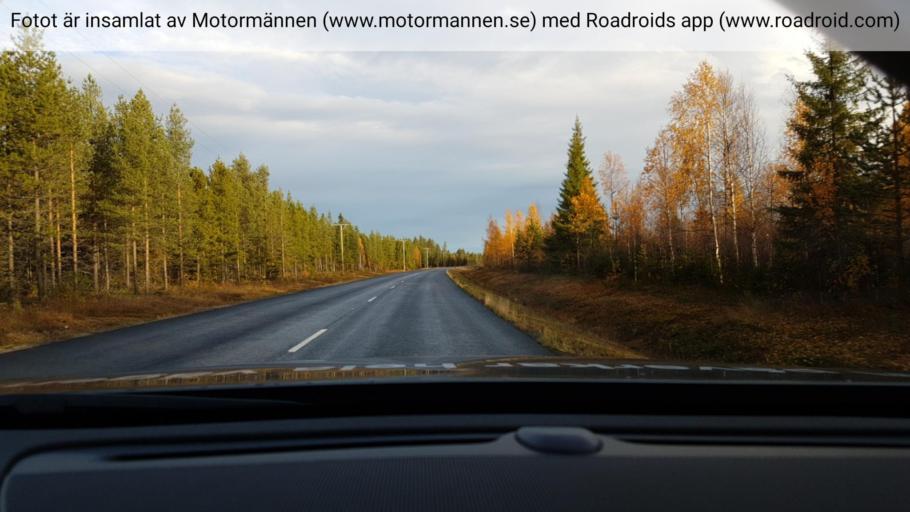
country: SE
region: Norrbotten
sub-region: Overkalix Kommun
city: OEverkalix
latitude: 66.9645
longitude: 22.6769
